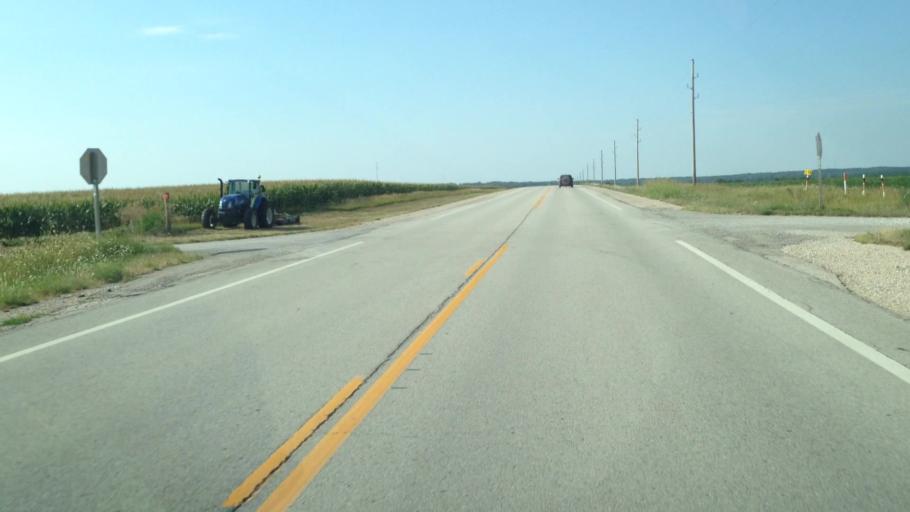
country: US
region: Kansas
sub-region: Anderson County
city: Garnett
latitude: 38.0521
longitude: -95.1695
